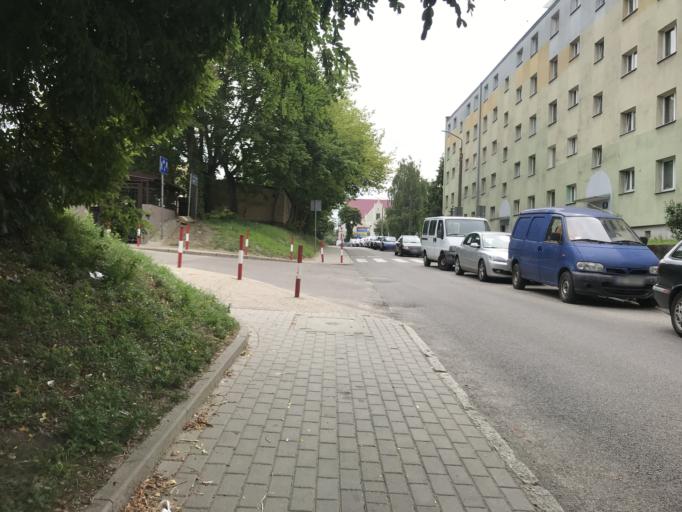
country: PL
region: Warmian-Masurian Voivodeship
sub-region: Powiat elblaski
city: Elblag
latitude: 54.1709
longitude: 19.4000
